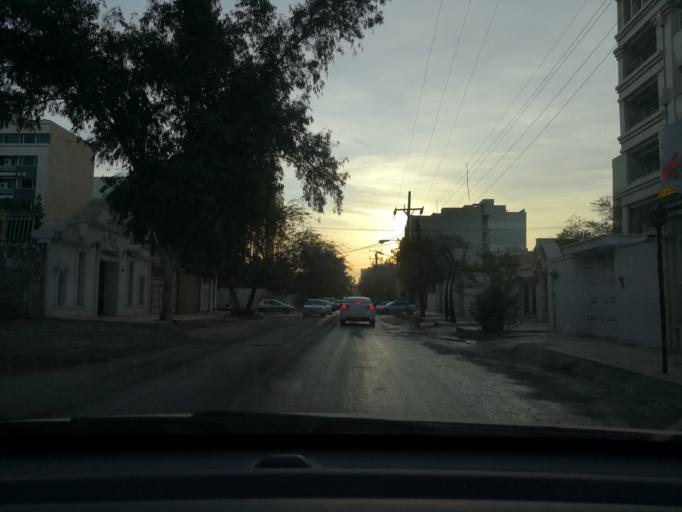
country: IR
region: Khuzestan
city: Ahvaz
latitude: 31.3509
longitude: 48.6842
